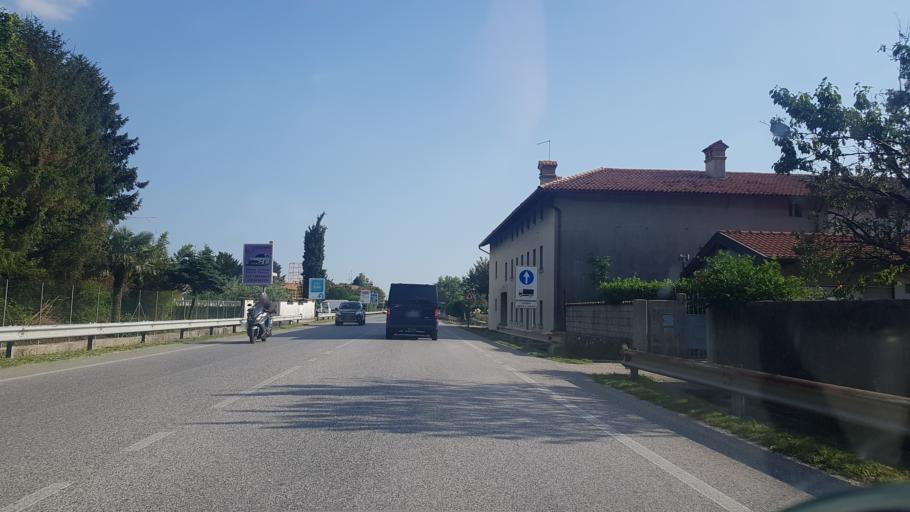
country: IT
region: Friuli Venezia Giulia
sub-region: Provincia di Udine
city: Gemona
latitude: 46.2754
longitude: 13.1086
